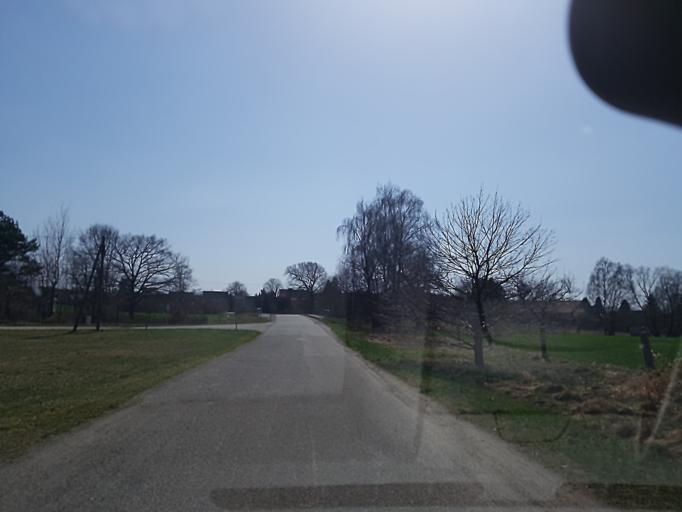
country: DE
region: Brandenburg
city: Schonborn
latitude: 51.5626
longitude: 13.4818
